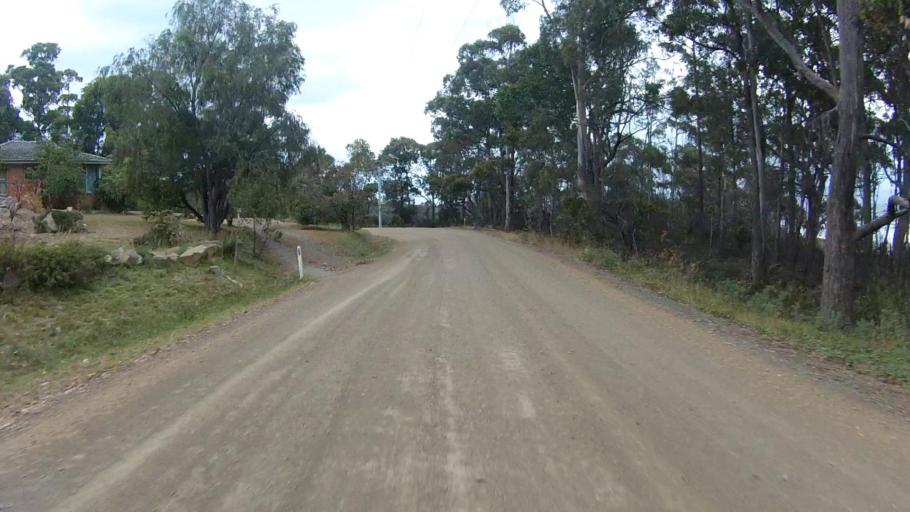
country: AU
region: Tasmania
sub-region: Huon Valley
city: Cygnet
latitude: -43.2275
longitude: 147.0960
